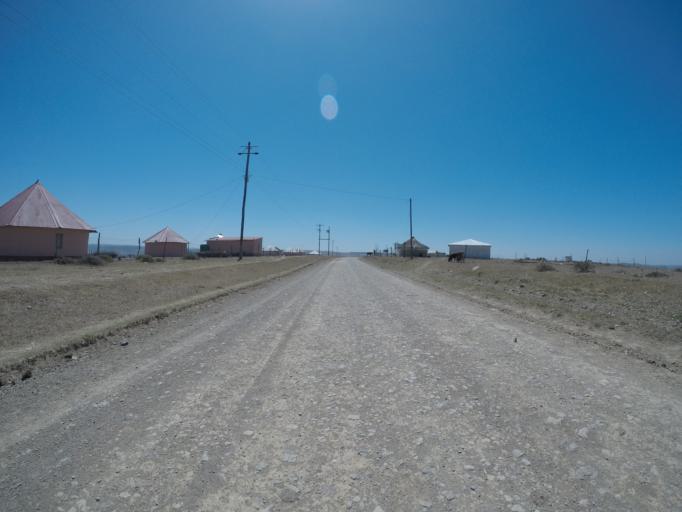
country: ZA
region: Eastern Cape
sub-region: OR Tambo District Municipality
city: Mthatha
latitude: -31.8843
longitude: 28.8750
